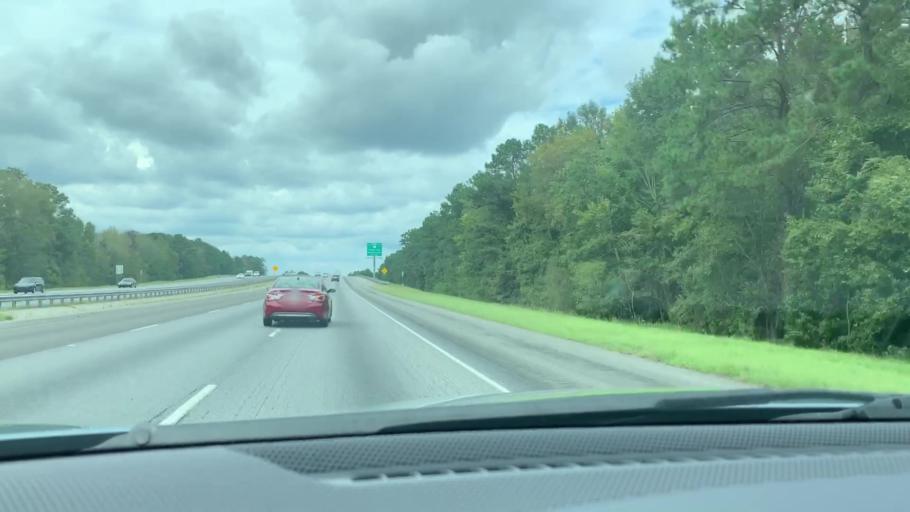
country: US
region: Georgia
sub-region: Bryan County
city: Richmond Hill
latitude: 31.9065
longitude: -81.3385
